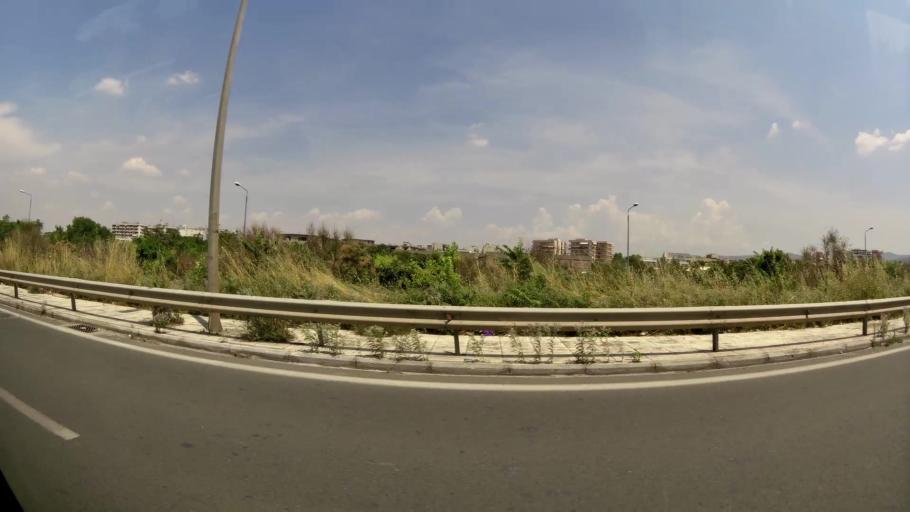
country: GR
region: Central Macedonia
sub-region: Nomos Thessalonikis
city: Menemeni
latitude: 40.6492
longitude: 22.9095
